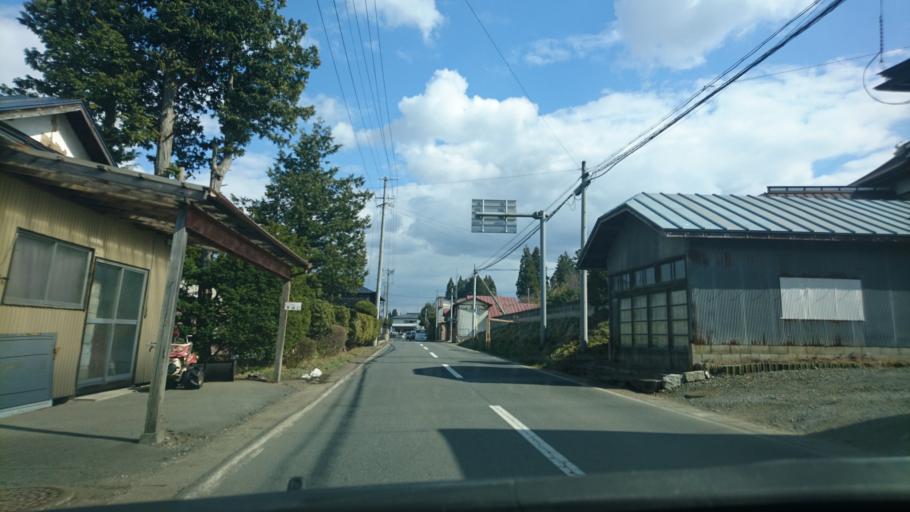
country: JP
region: Iwate
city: Kitakami
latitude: 39.2970
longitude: 141.2018
